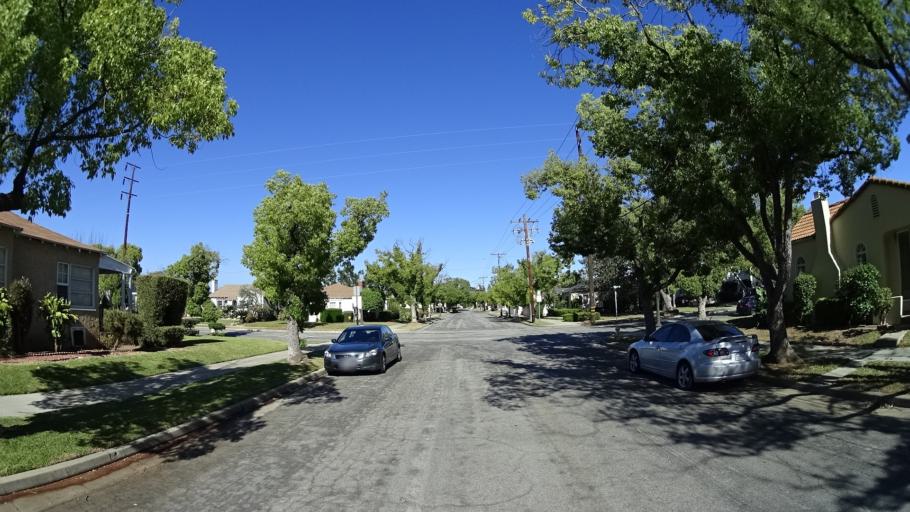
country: US
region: California
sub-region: Los Angeles County
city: Monterey Park
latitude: 34.0739
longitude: -118.1468
